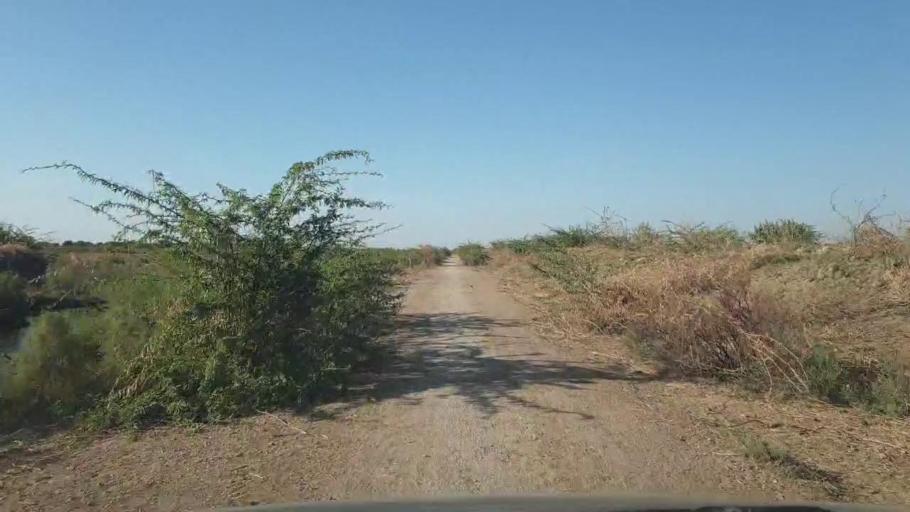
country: PK
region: Sindh
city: Dhoro Naro
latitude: 25.4317
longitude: 69.5527
